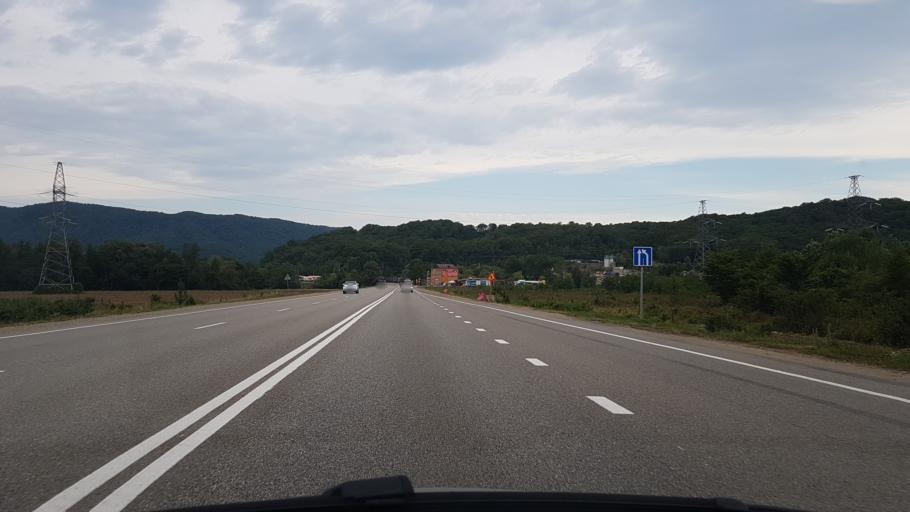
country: RU
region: Krasnodarskiy
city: Lermontovo
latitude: 44.4429
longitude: 38.7868
